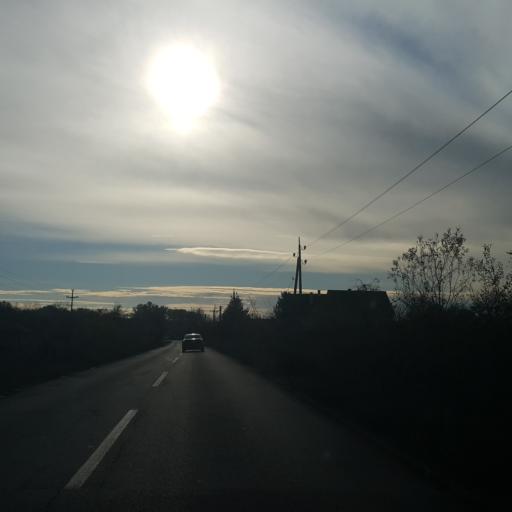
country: RS
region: Central Serbia
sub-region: Belgrade
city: Lazarevac
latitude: 44.4103
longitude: 20.2676
